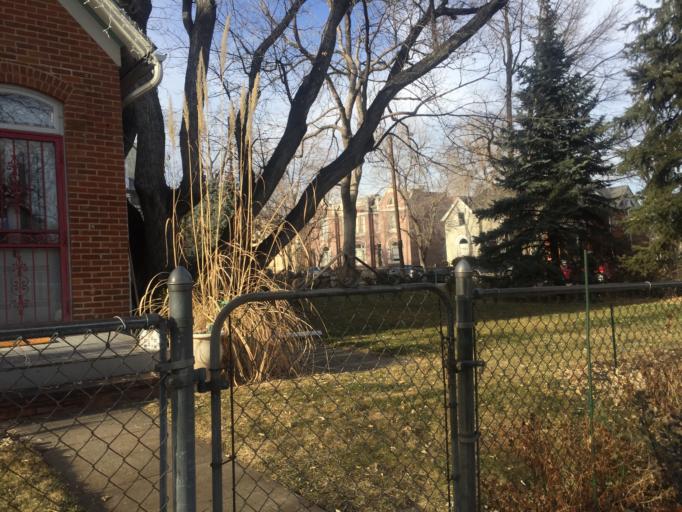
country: US
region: Colorado
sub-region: Denver County
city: Denver
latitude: 39.7561
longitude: -104.9801
